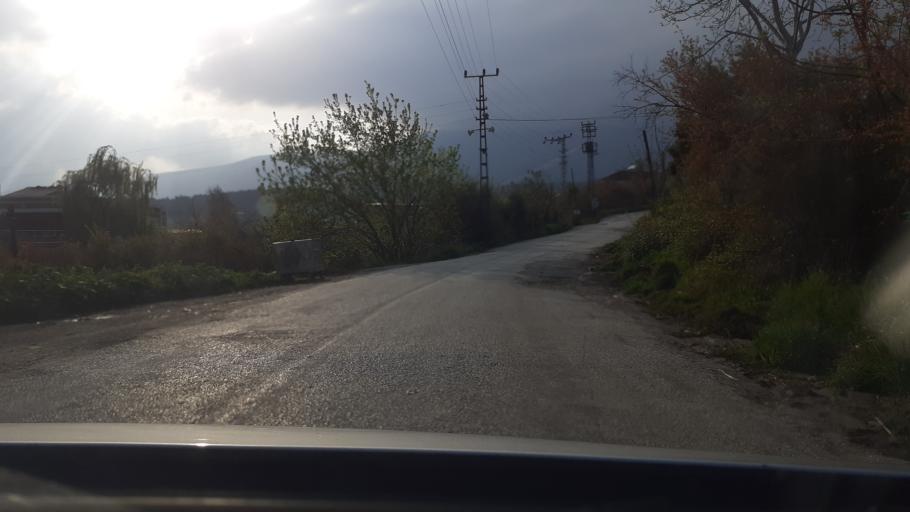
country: TR
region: Hatay
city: Kirikhan
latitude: 36.4997
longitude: 36.3330
